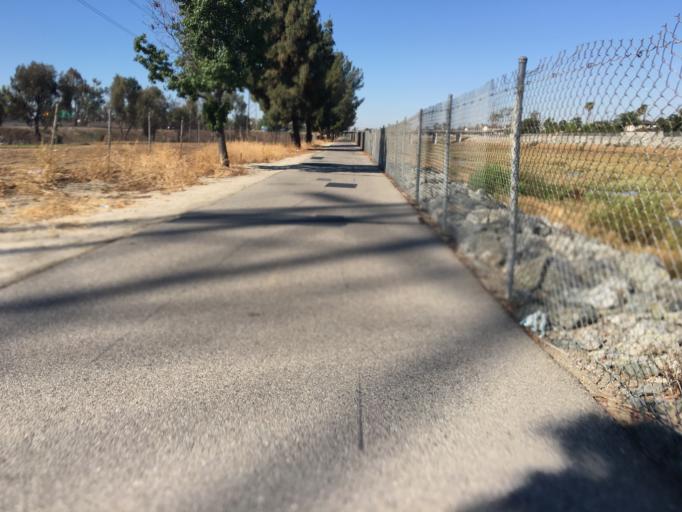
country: US
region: California
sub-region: Los Angeles County
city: Santa Fe Springs
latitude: 33.9537
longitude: -118.0906
